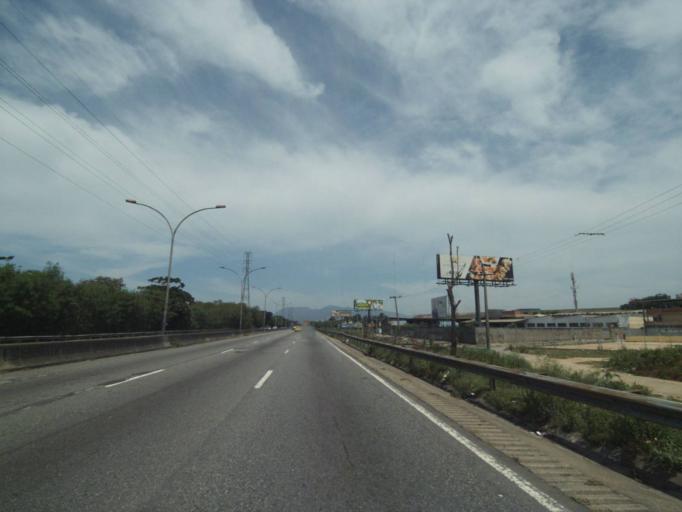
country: BR
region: Rio de Janeiro
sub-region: Duque De Caxias
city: Duque de Caxias
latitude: -22.8024
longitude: -43.3355
